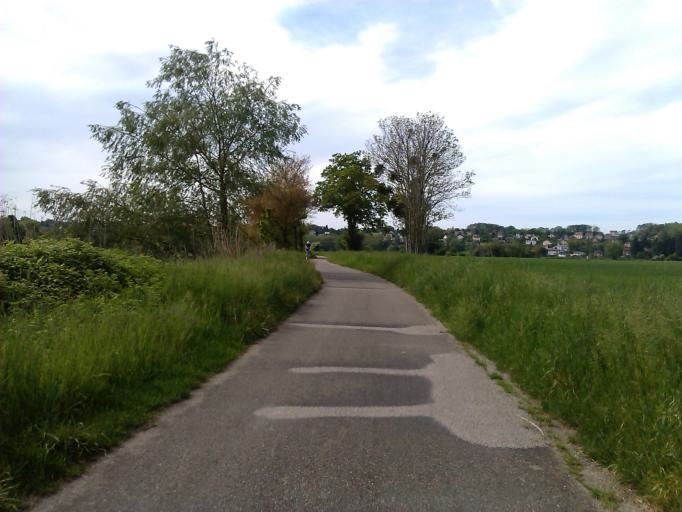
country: FR
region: Franche-Comte
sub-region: Departement du Doubs
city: Saint-Vit
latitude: 47.1703
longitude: 5.8107
